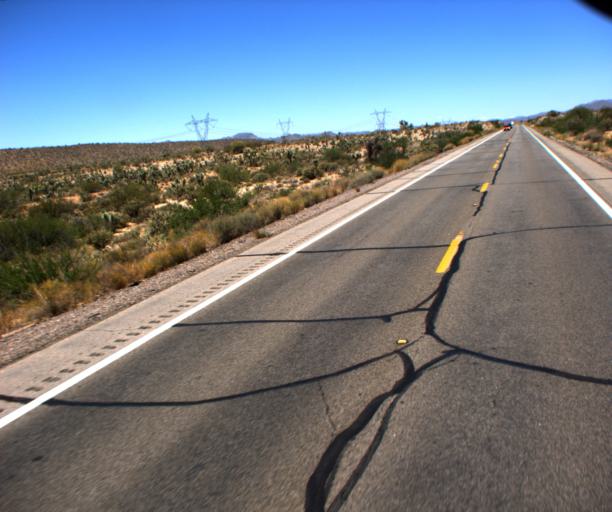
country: US
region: Arizona
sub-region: Yavapai County
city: Bagdad
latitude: 34.3288
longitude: -113.1415
